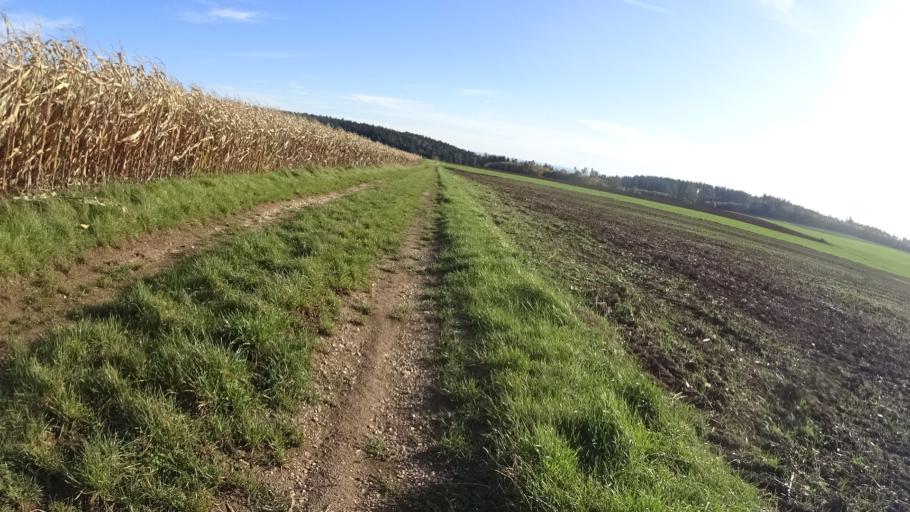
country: DE
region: Bavaria
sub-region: Upper Bavaria
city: Bohmfeld
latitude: 48.8551
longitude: 11.3617
